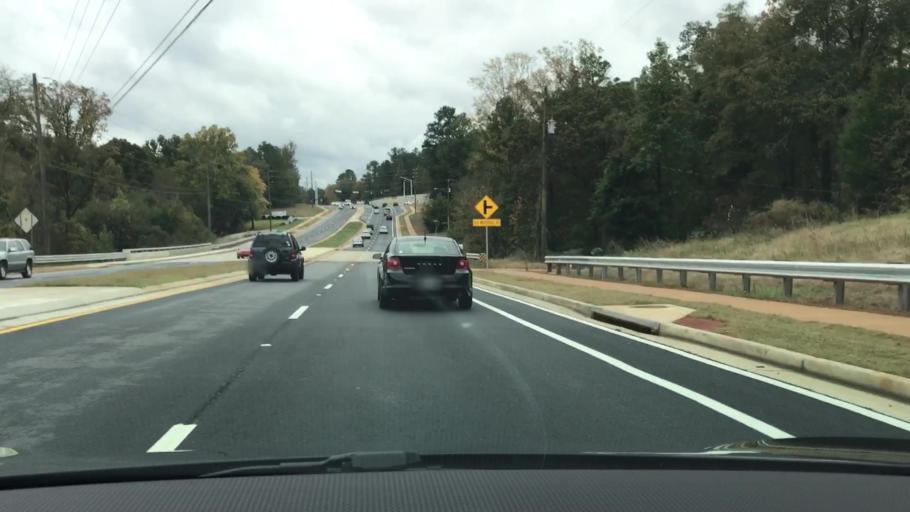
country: US
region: Georgia
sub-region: Oconee County
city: Watkinsville
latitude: 33.9029
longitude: -83.4635
